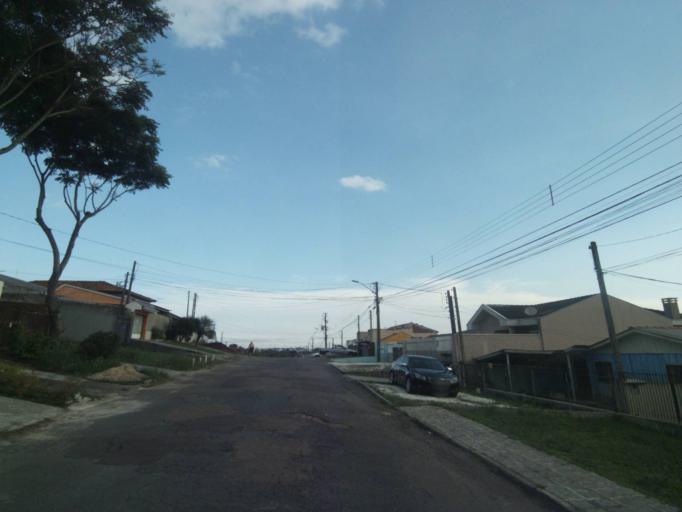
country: BR
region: Parana
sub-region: Pinhais
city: Pinhais
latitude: -25.4077
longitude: -49.2008
